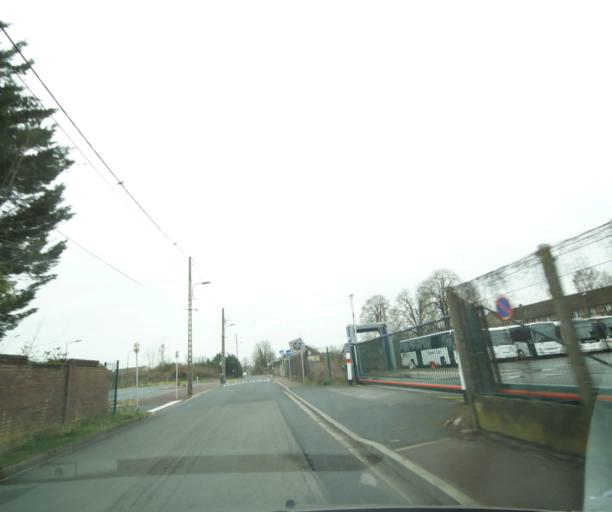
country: FR
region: Picardie
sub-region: Departement de l'Oise
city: Noyon
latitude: 49.5753
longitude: 3.0128
